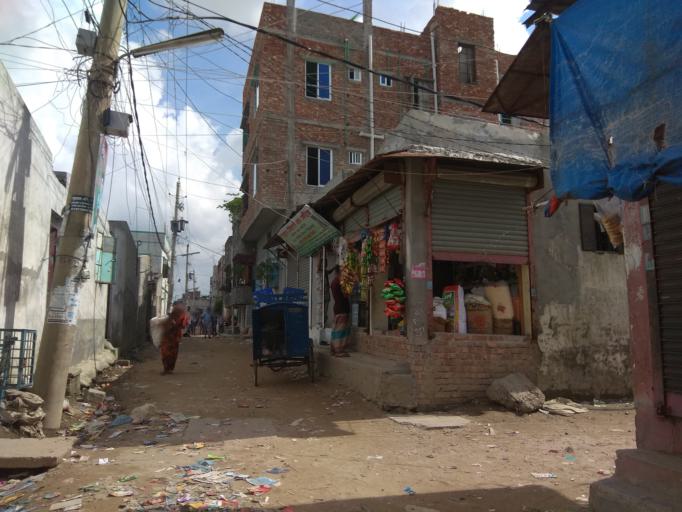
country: BD
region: Dhaka
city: Paltan
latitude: 23.8094
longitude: 90.3849
